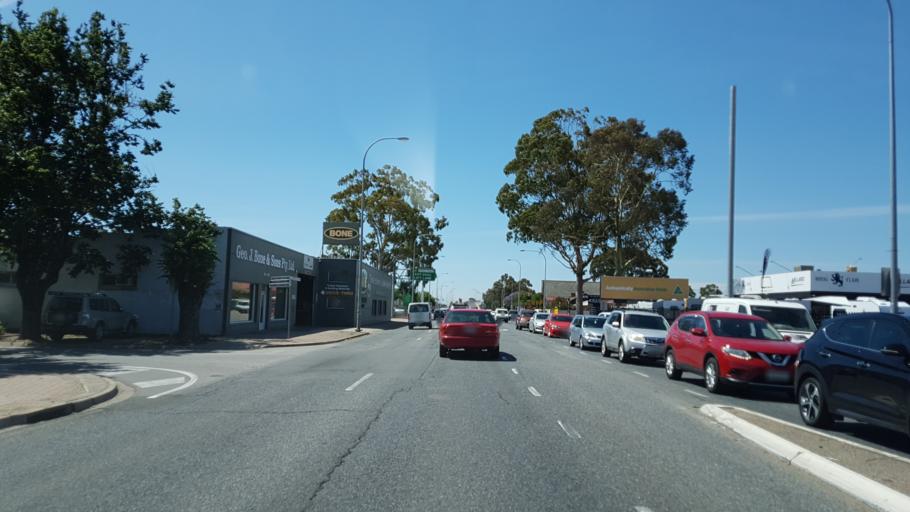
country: AU
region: South Australia
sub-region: Mitcham
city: Clarence Gardens
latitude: -34.9722
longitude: 138.5733
